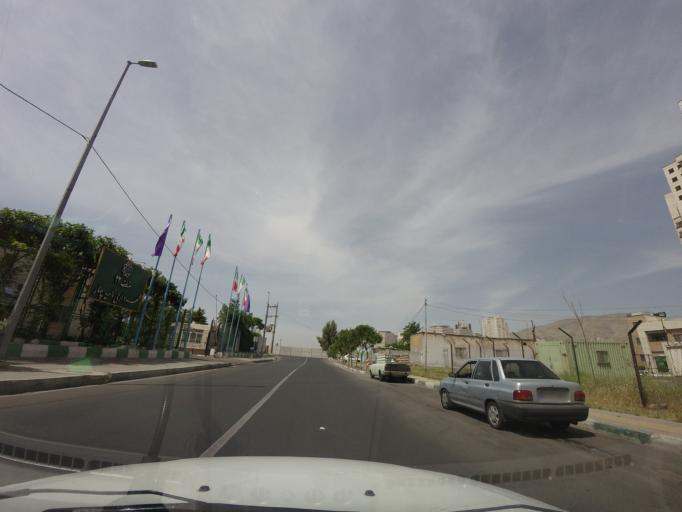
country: IR
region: Tehran
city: Shahr-e Qods
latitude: 35.7465
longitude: 51.1948
